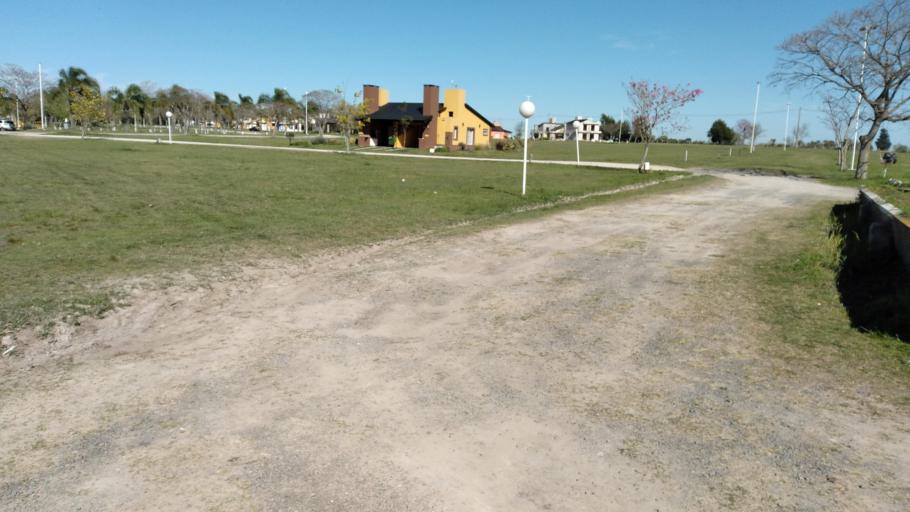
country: AR
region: Entre Rios
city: Villa Maria Grande
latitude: -31.6570
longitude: -59.9298
